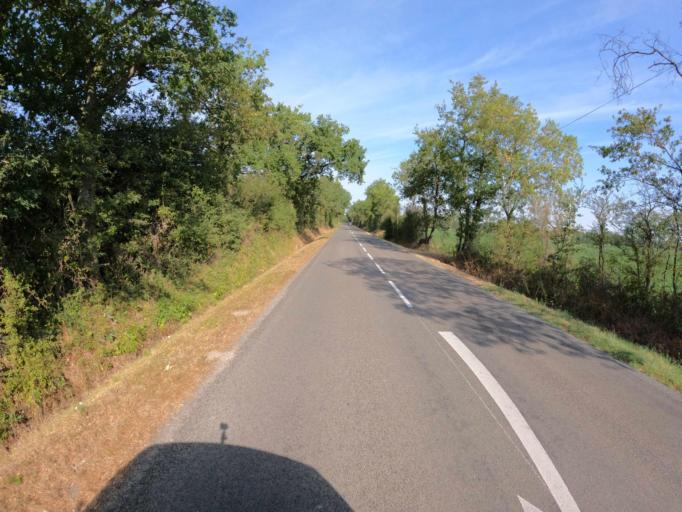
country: FR
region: Pays de la Loire
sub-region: Departement de la Vendee
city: Saint-Christophe-du-Ligneron
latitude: 46.8010
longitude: -1.7939
